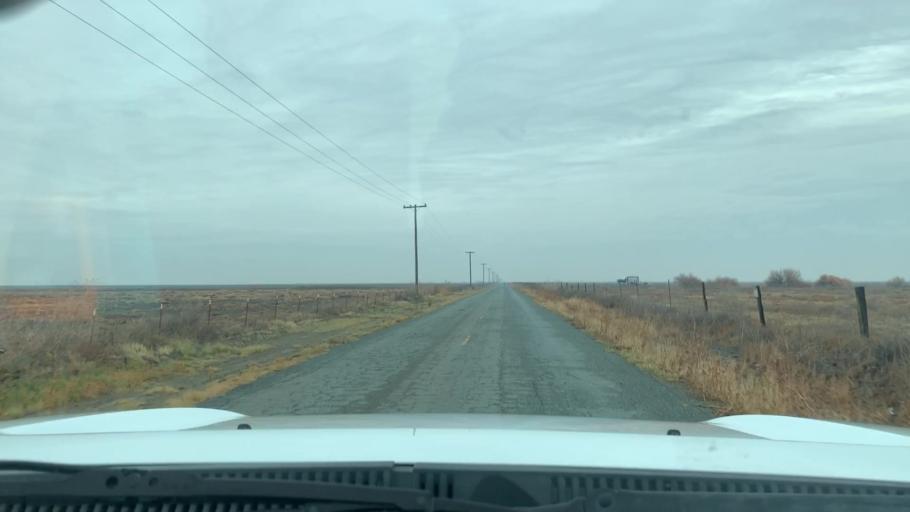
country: US
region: California
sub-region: Tulare County
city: Alpaugh
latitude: 35.7609
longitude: -119.5415
